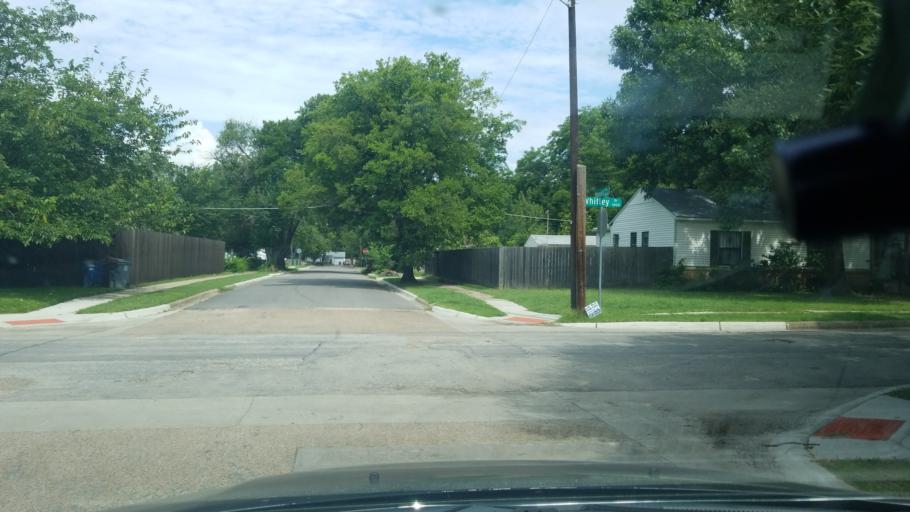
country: US
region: Texas
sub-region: Dallas County
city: Balch Springs
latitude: 32.7355
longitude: -96.6916
